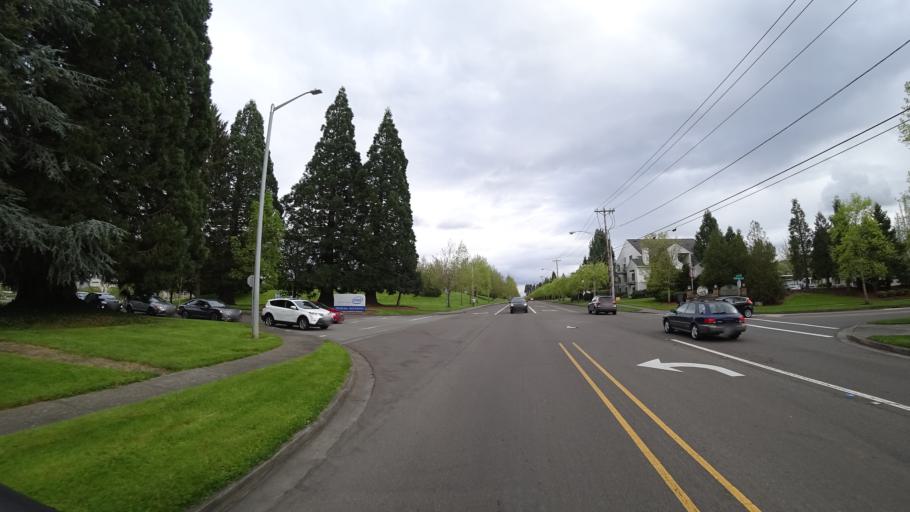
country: US
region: Oregon
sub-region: Washington County
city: Hillsboro
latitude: 45.5456
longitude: -122.9663
